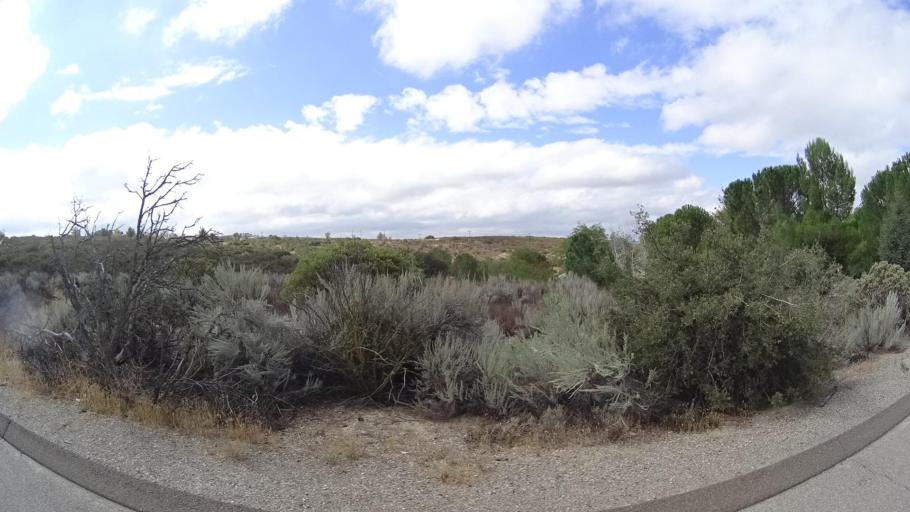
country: US
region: California
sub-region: San Diego County
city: Campo
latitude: 32.6709
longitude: -116.3175
